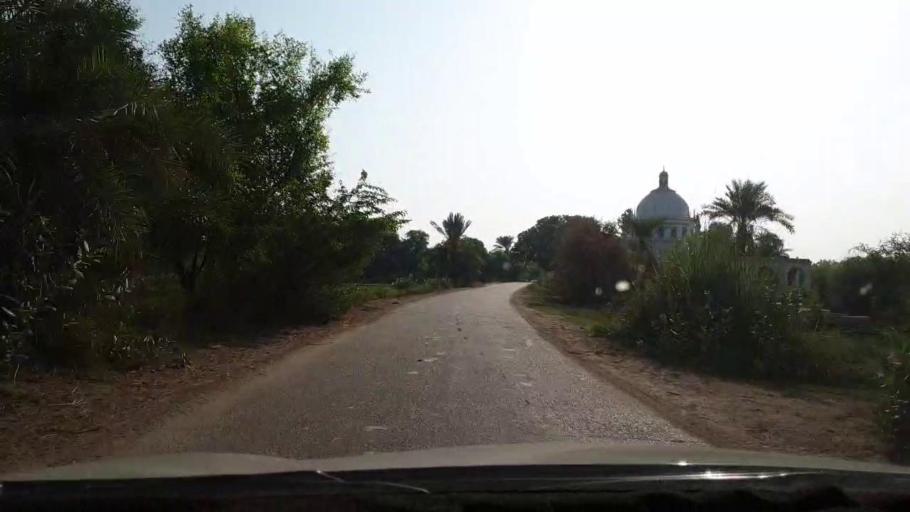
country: PK
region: Sindh
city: Larkana
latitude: 27.5499
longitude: 68.2497
